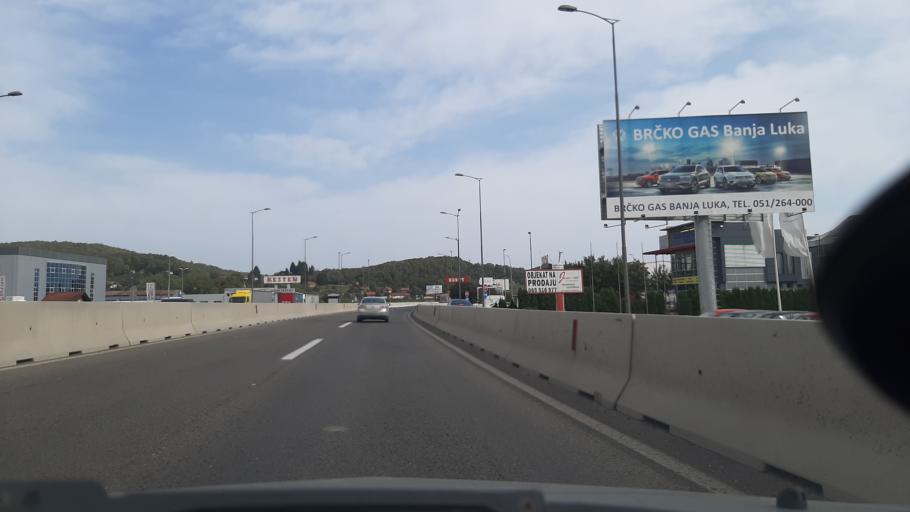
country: BA
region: Republika Srpska
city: Trn
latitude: 44.8694
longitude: 17.2528
